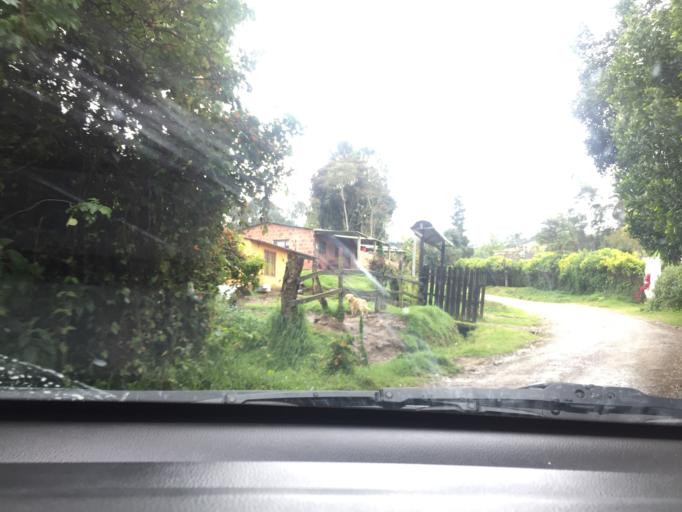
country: CO
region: Cundinamarca
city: El Rosal
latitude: 4.8583
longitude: -74.2934
